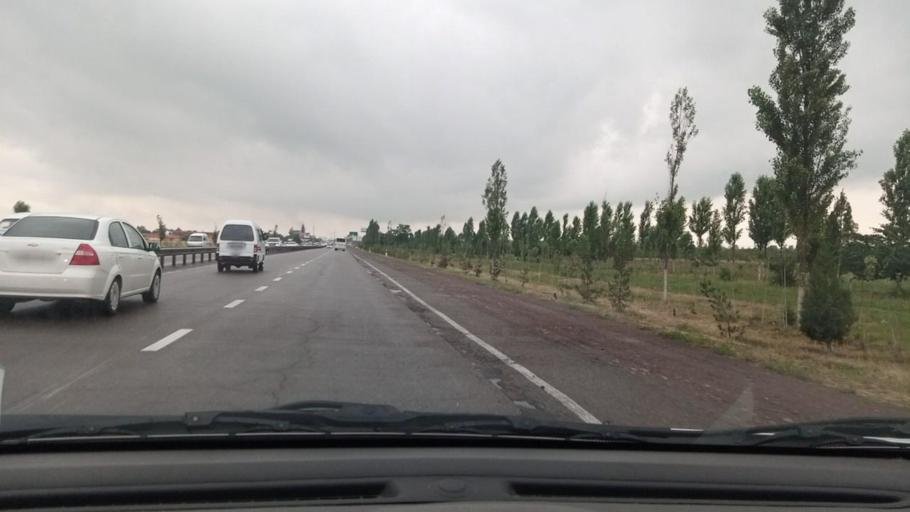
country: UZ
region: Toshkent
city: Ohangaron
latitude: 40.9165
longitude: 69.6051
